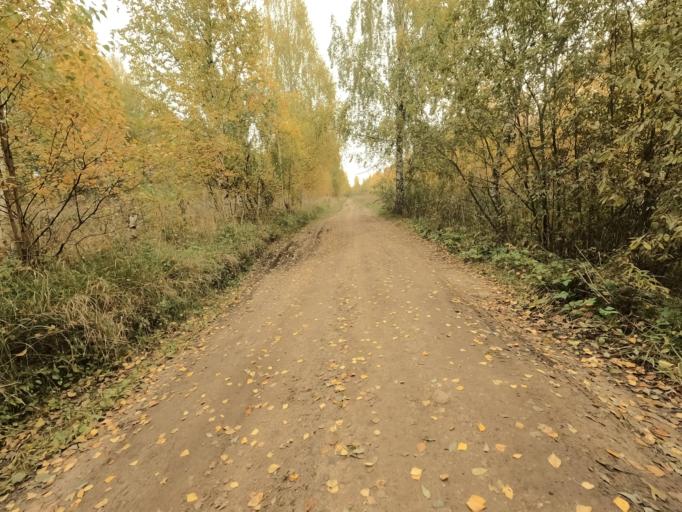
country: RU
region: Novgorod
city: Pankovka
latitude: 58.8663
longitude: 30.9241
